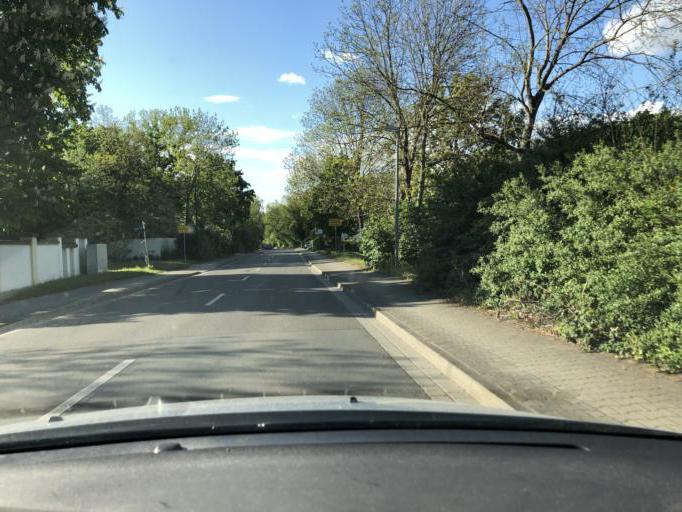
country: DE
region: Saxony
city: Markkleeberg
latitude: 51.2438
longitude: 12.3846
